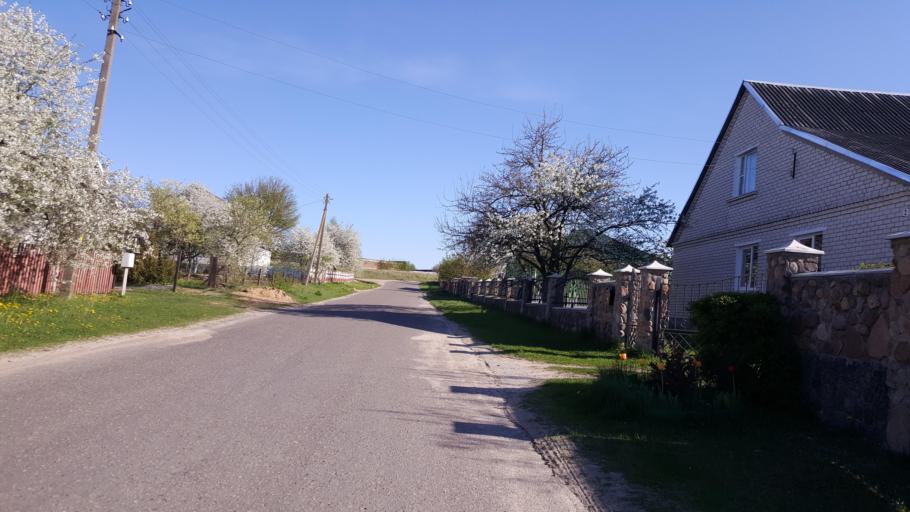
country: BY
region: Brest
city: Kamyanyets
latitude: 52.4060
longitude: 23.8351
